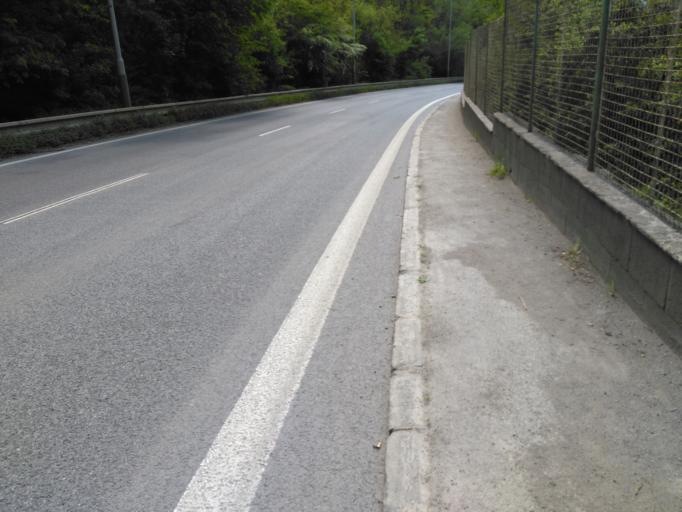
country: CZ
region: Central Bohemia
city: Cernosice
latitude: 49.9968
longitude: 14.3426
